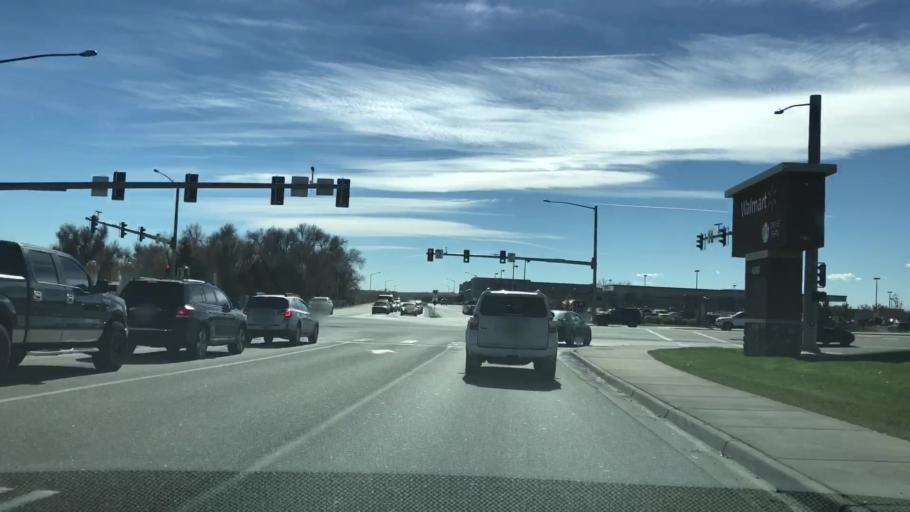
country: US
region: Colorado
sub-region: Weld County
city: Windsor
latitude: 40.5237
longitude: -104.9885
